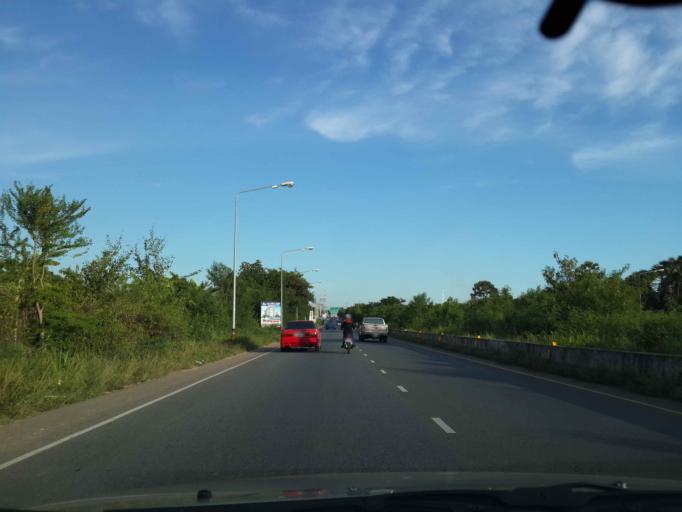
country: TH
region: Chon Buri
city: Phatthaya
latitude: 12.8874
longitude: 100.9024
